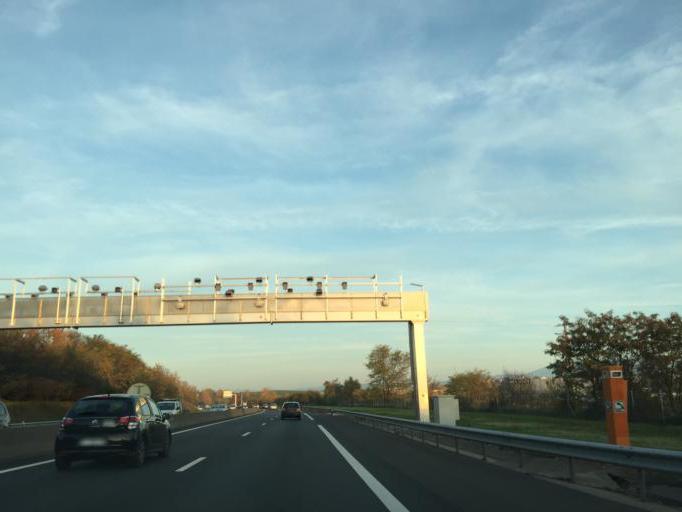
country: FR
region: Rhone-Alpes
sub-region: Departement de la Loire
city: Saint-Chamond
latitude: 45.4918
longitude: 4.5186
